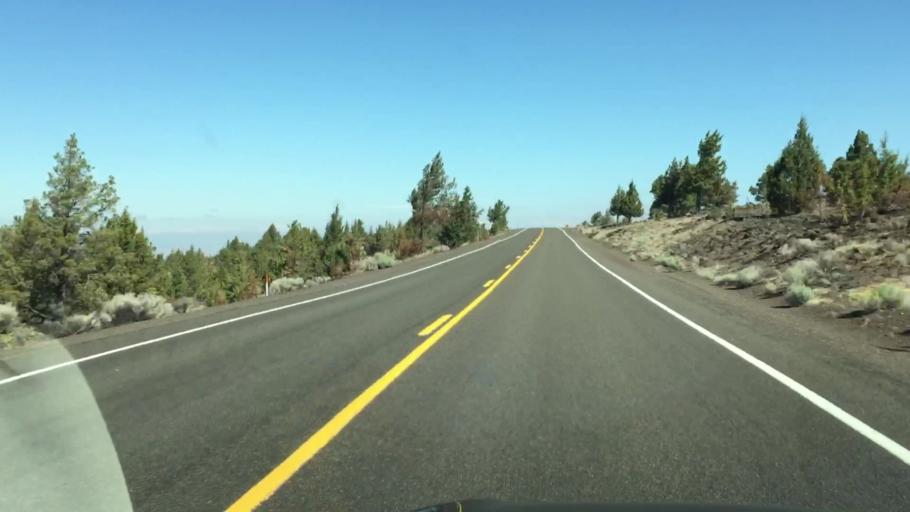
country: US
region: Oregon
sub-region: Jefferson County
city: Warm Springs
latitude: 45.0820
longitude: -121.0255
